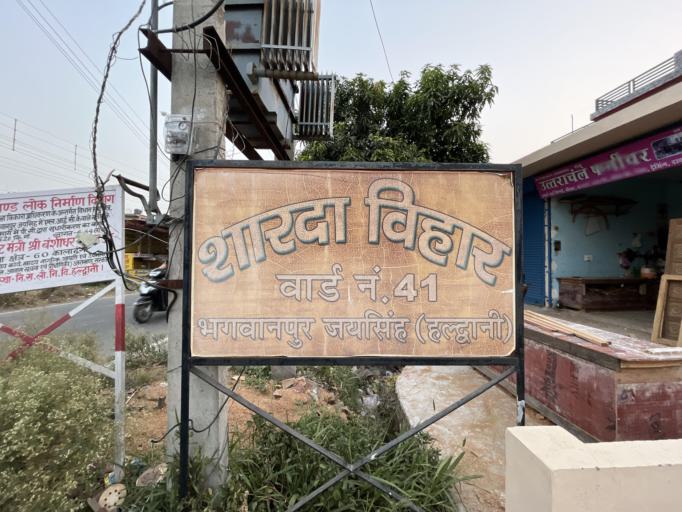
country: IN
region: Uttarakhand
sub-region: Naini Tal
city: Haldwani
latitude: 29.2226
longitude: 79.4788
